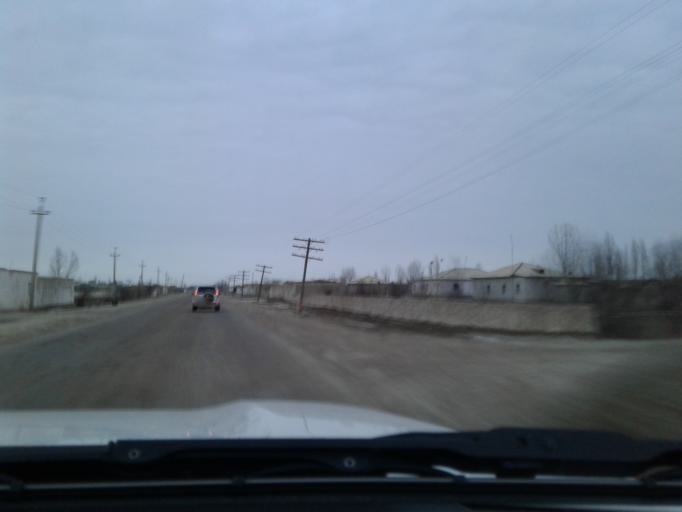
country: TM
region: Dasoguz
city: Dasoguz
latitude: 42.0091
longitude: 59.8858
